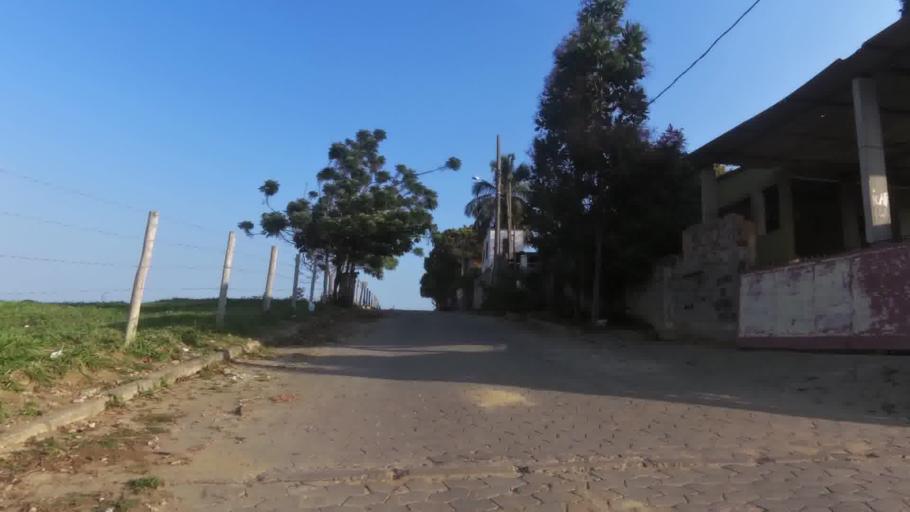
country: BR
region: Espirito Santo
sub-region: Piuma
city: Piuma
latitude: -20.8268
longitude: -40.7186
